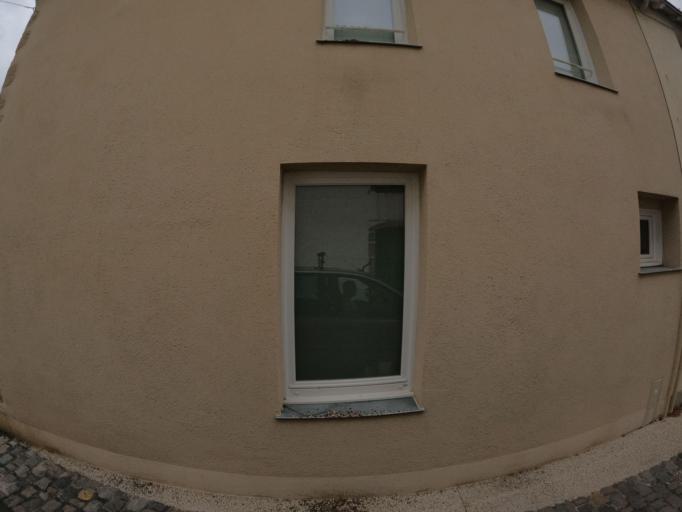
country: FR
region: Pays de la Loire
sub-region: Departement de la Vendee
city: Tiffauges
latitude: 47.0133
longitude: -1.1119
